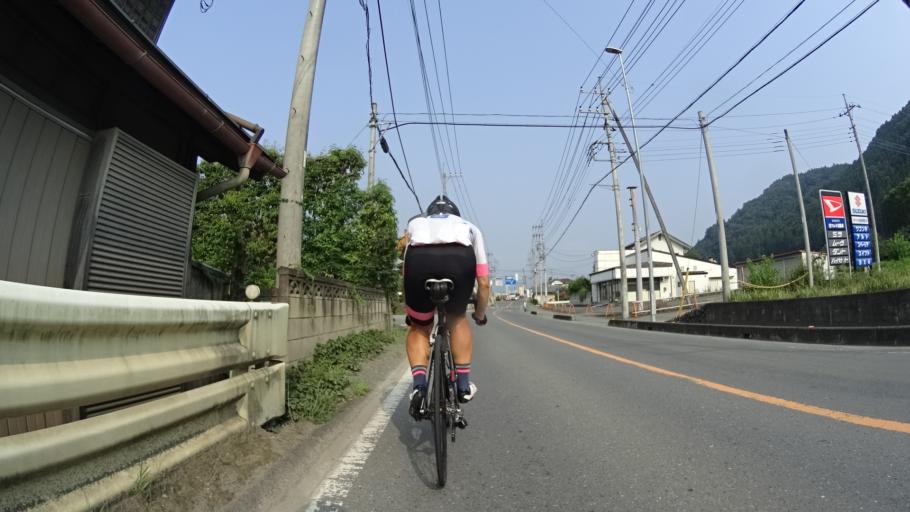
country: JP
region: Saitama
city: Chichibu
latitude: 36.0126
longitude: 139.0232
